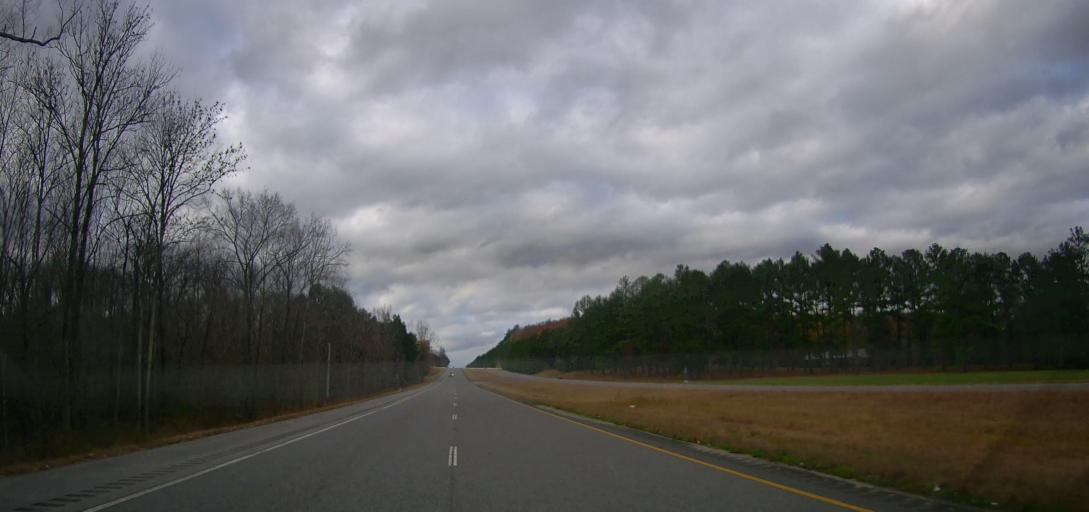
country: US
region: Alabama
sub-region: Lawrence County
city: Town Creek
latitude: 34.6127
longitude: -87.4592
